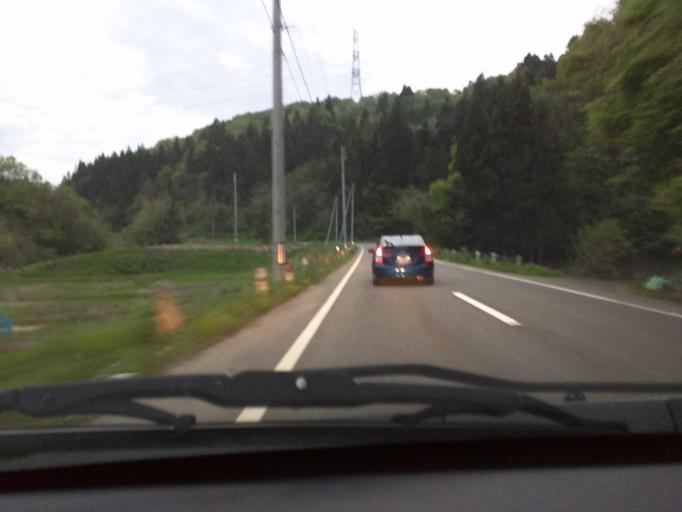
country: JP
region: Niigata
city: Ojiya
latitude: 37.3212
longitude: 138.6916
